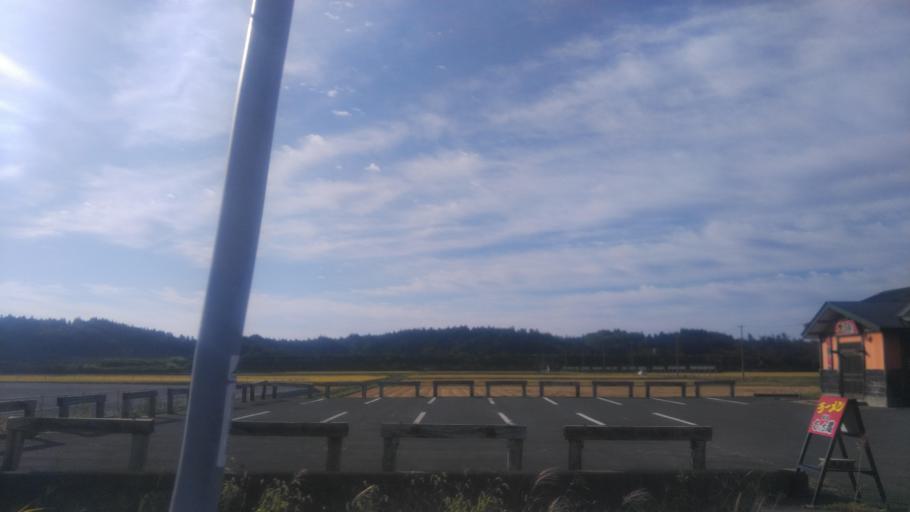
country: JP
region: Akita
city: Noshiromachi
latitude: 40.1883
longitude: 140.0772
